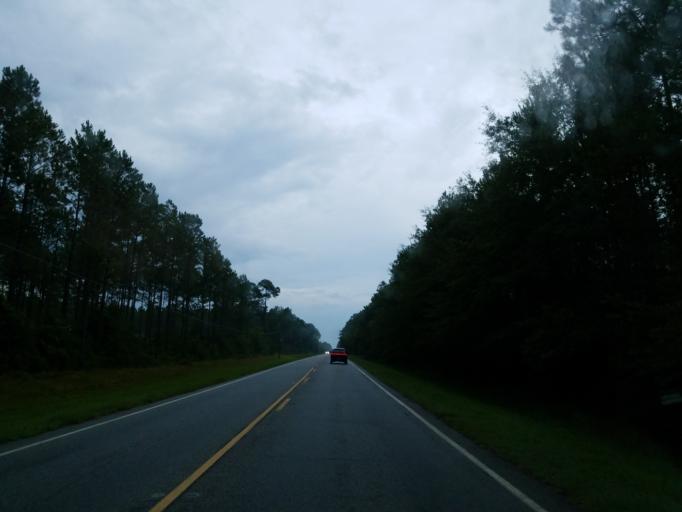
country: US
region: Georgia
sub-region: Lanier County
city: Lakeland
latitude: 31.0532
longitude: -83.1385
